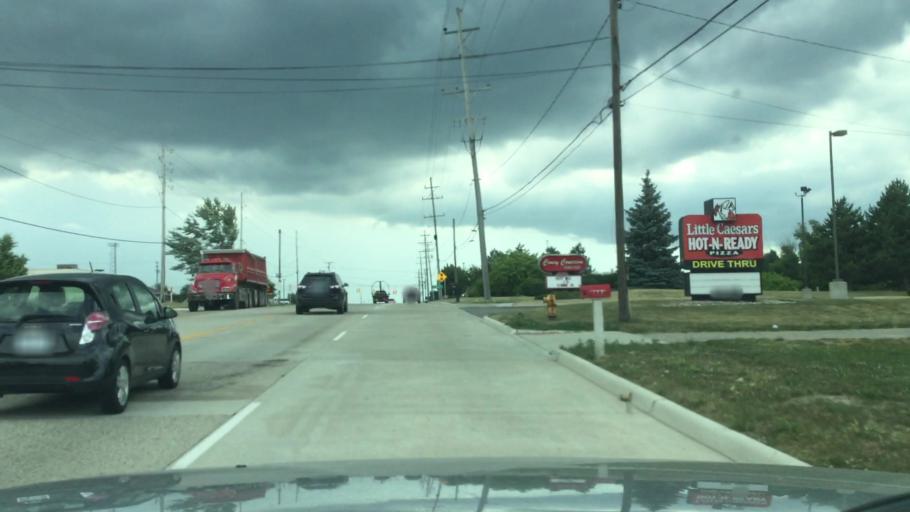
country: US
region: Michigan
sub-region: Genesee County
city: Swartz Creek
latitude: 43.0046
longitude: -83.7729
